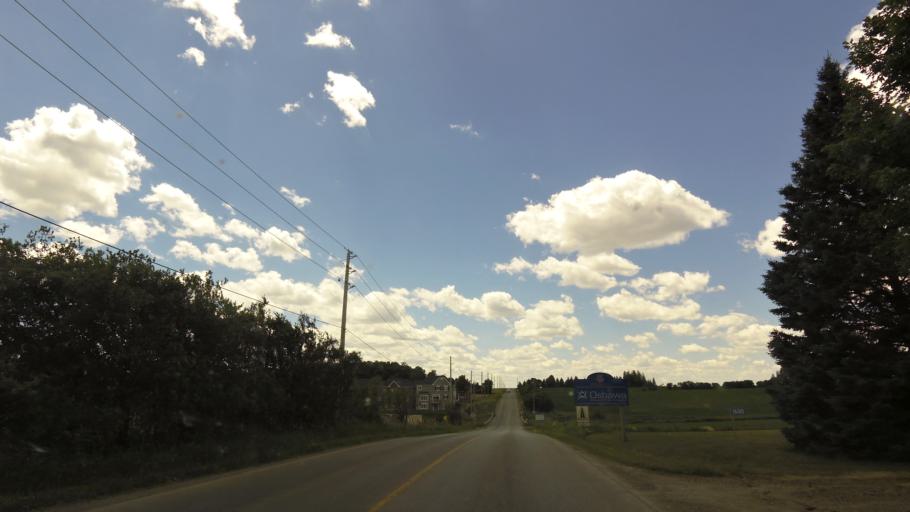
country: CA
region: Ontario
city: Oshawa
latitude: 43.9612
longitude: -78.8381
